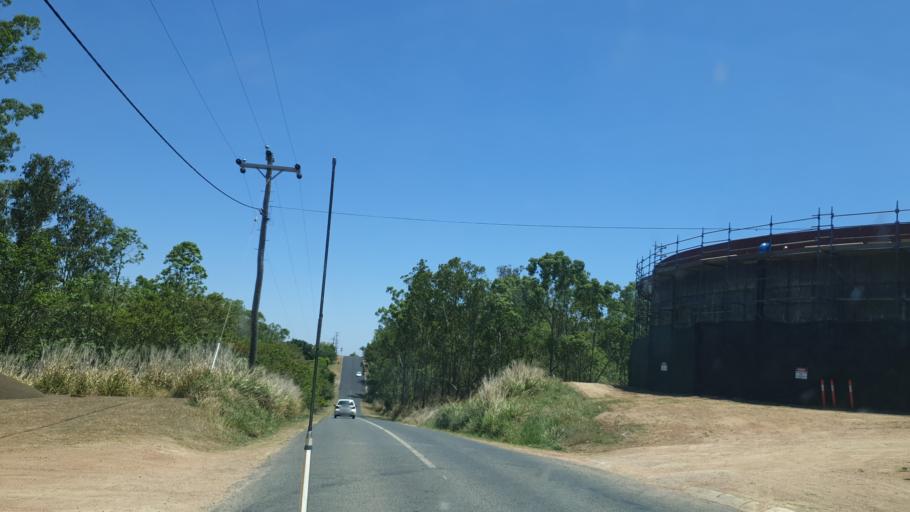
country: AU
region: Queensland
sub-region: Tablelands
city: Atherton
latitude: -17.2663
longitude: 145.4905
